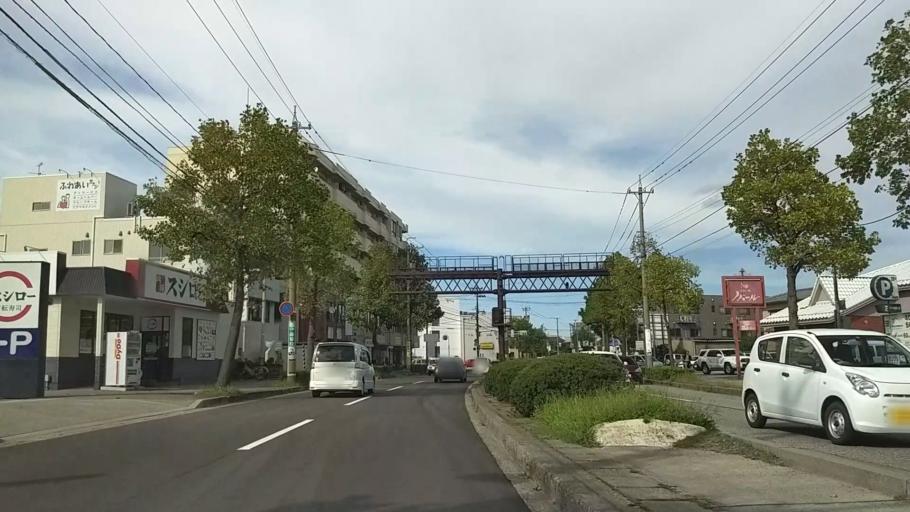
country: JP
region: Ishikawa
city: Nonoichi
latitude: 36.5420
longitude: 136.6395
